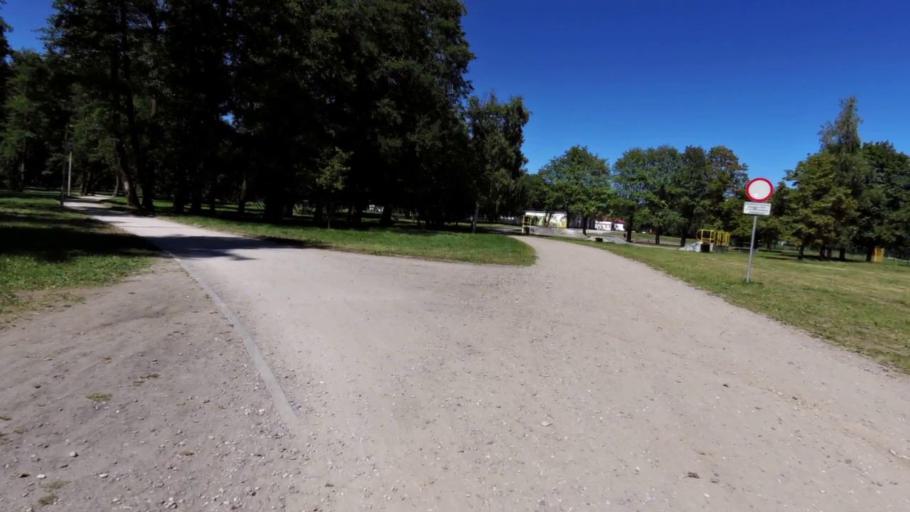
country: PL
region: West Pomeranian Voivodeship
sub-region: Powiat szczecinecki
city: Szczecinek
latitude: 53.6976
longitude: 16.6942
